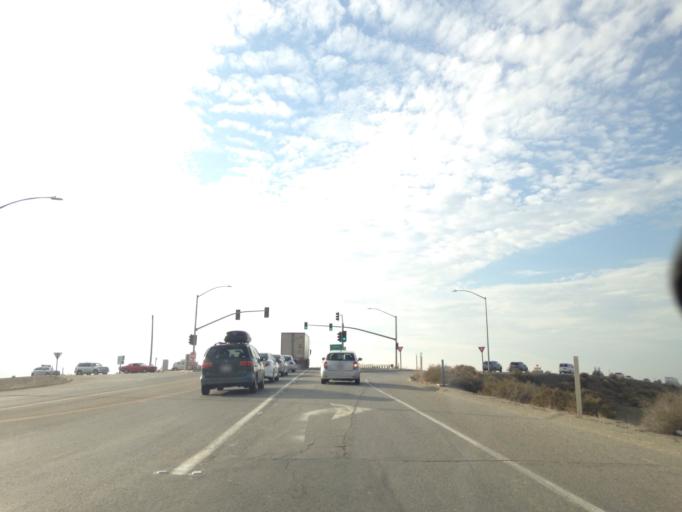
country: US
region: California
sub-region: Kern County
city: Lost Hills
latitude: 35.6164
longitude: -119.6499
